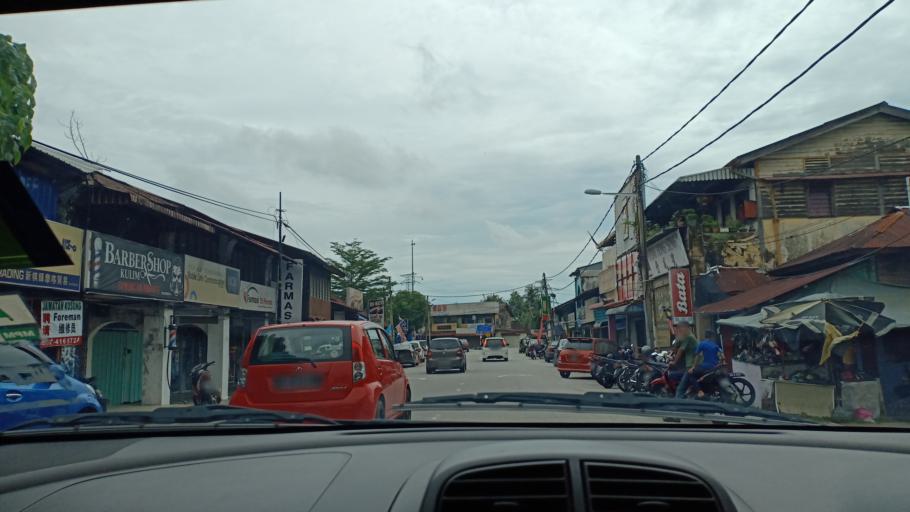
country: MY
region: Penang
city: Bukit Mertajam
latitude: 5.4040
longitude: 100.4648
